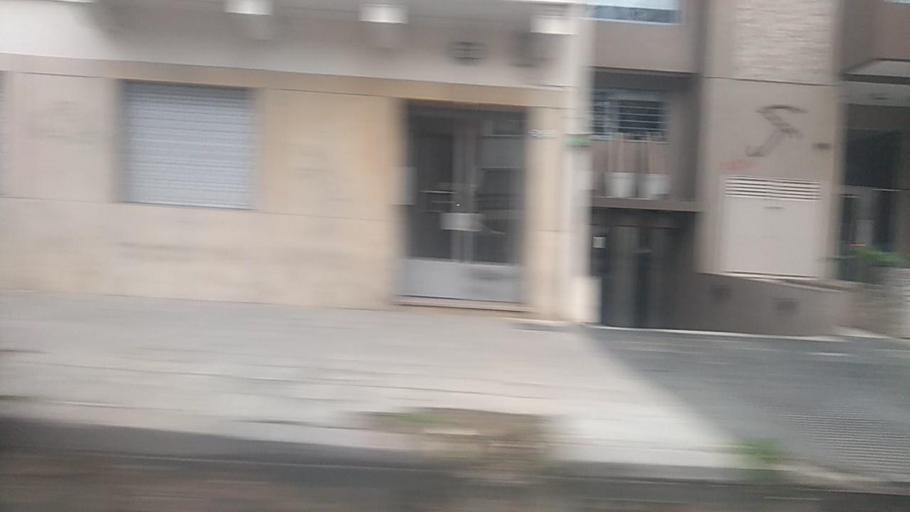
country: AR
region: Buenos Aires F.D.
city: Villa Santa Rita
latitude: -34.6009
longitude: -58.4976
